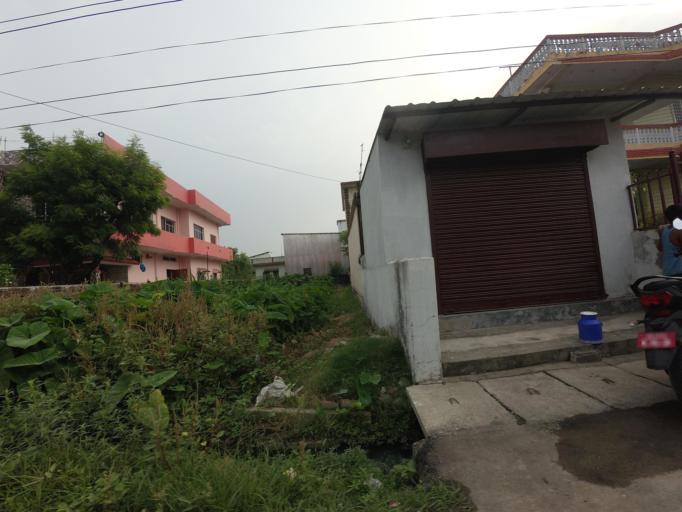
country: NP
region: Western Region
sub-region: Lumbini Zone
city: Bhairahawa
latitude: 27.5238
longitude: 83.4543
